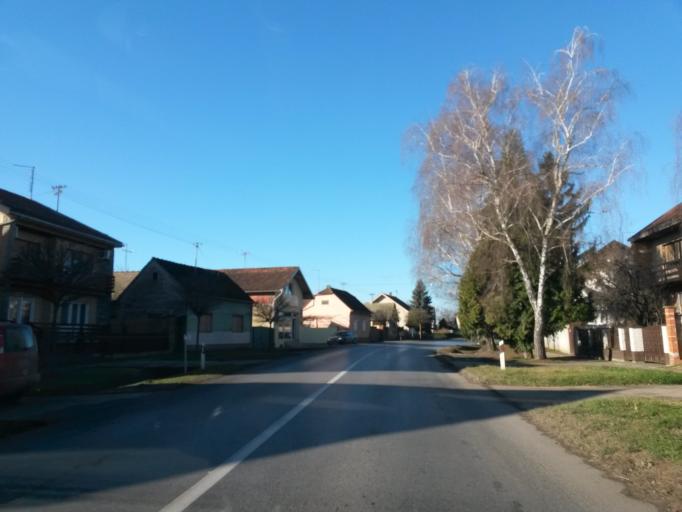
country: HR
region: Osjecko-Baranjska
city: Petrijevci
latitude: 45.6141
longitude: 18.5381
